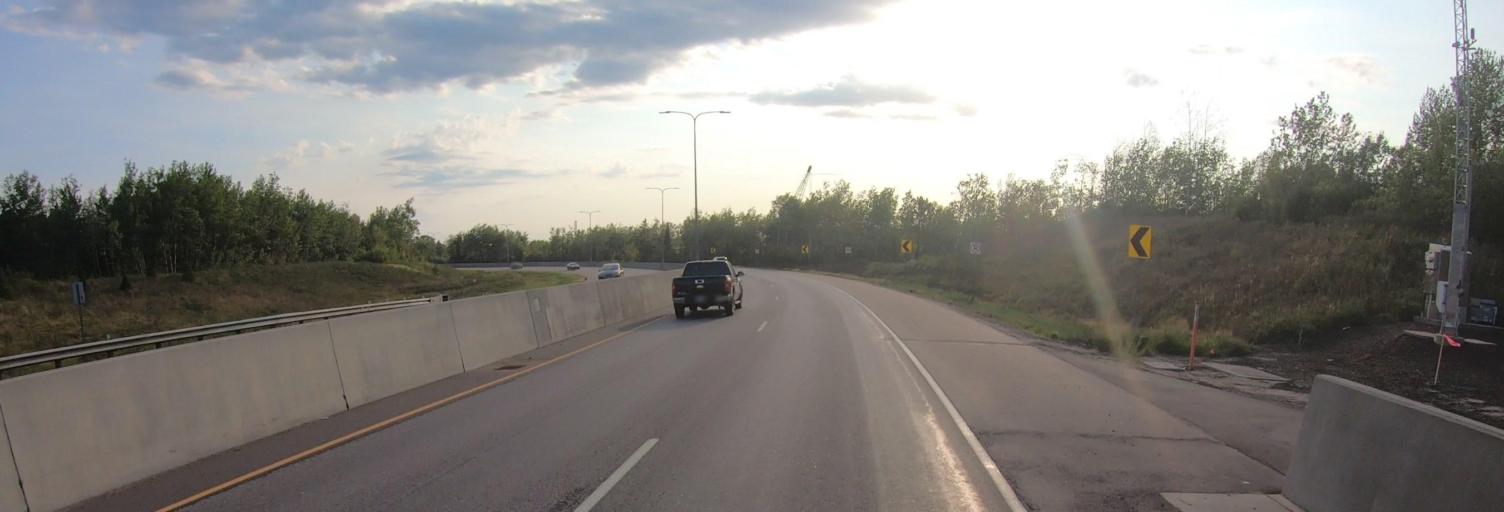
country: US
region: Minnesota
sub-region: Saint Louis County
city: Virginia
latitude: 47.5158
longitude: -92.5258
